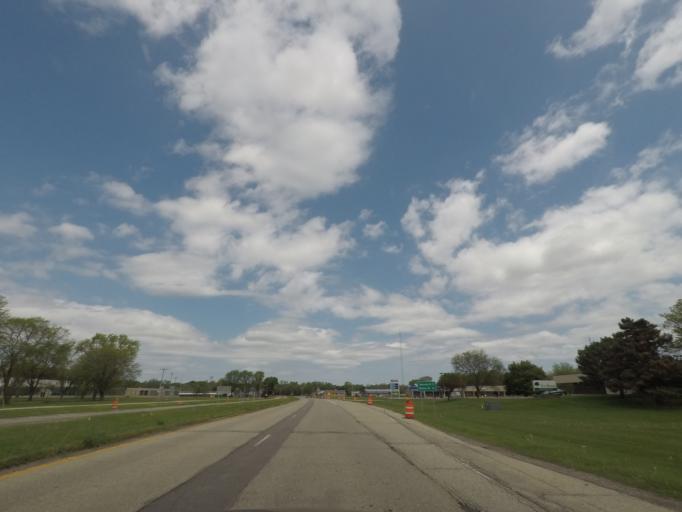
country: US
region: Illinois
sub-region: Winnebago County
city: South Beloit
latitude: 42.4933
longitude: -89.0196
